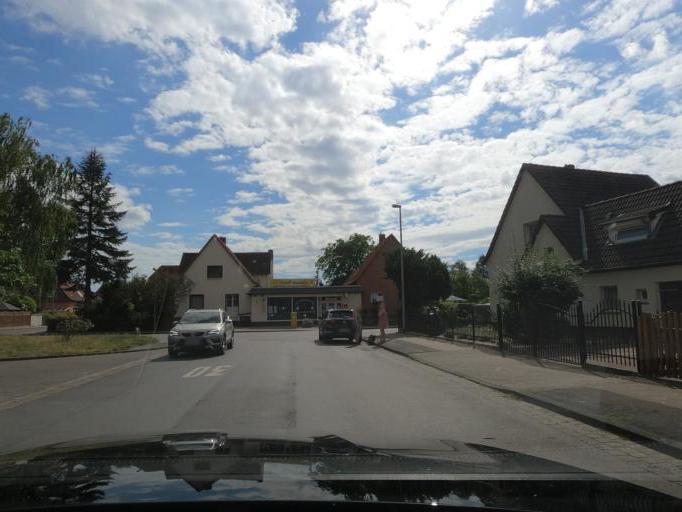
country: DE
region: Lower Saxony
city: Isernhagen Farster Bauerschaft
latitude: 52.3977
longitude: 9.8324
